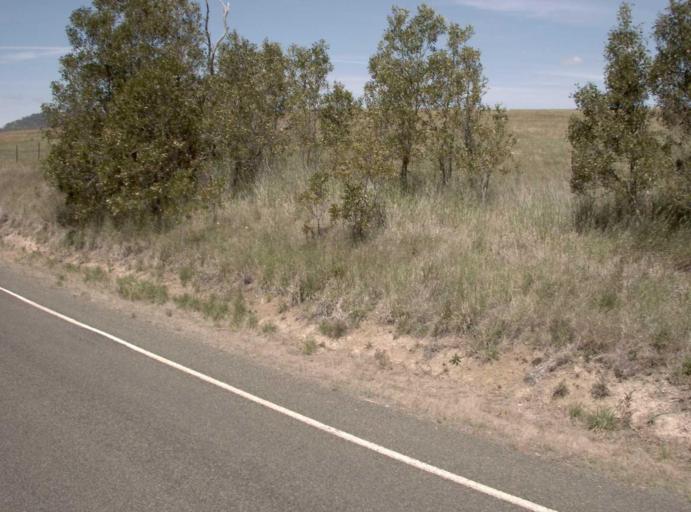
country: AU
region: Victoria
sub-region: Alpine
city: Mount Beauty
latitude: -37.1423
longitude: 147.6469
